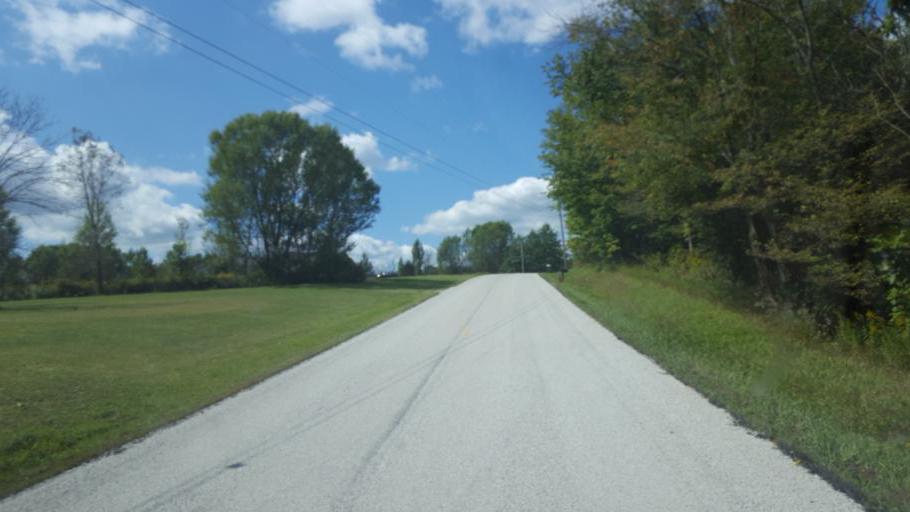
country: US
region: Ohio
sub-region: Ashland County
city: Ashland
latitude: 40.9680
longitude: -82.2601
